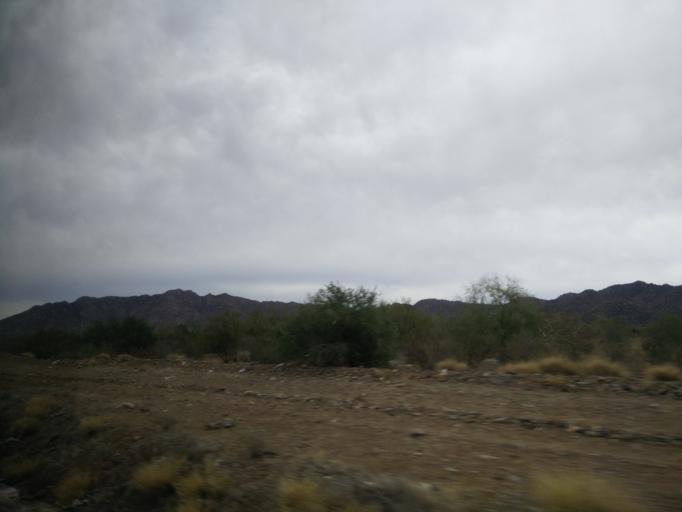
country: MX
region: Sonora
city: Hermosillo
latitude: 28.9484
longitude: -110.9622
